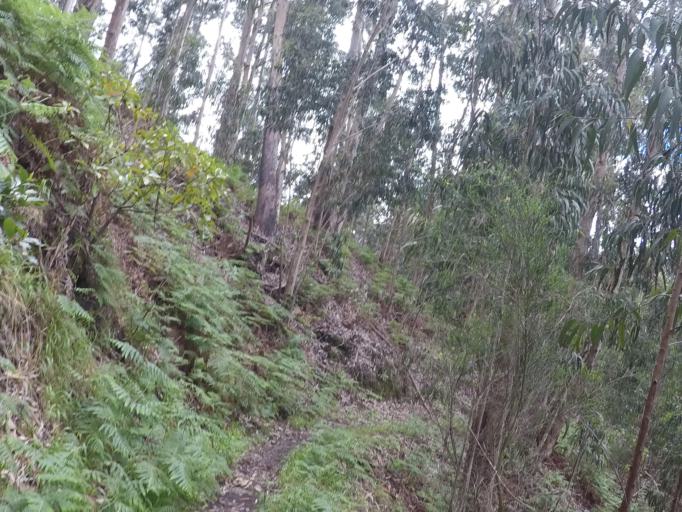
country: PT
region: Madeira
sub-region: Camara de Lobos
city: Curral das Freiras
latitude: 32.7476
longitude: -17.0161
